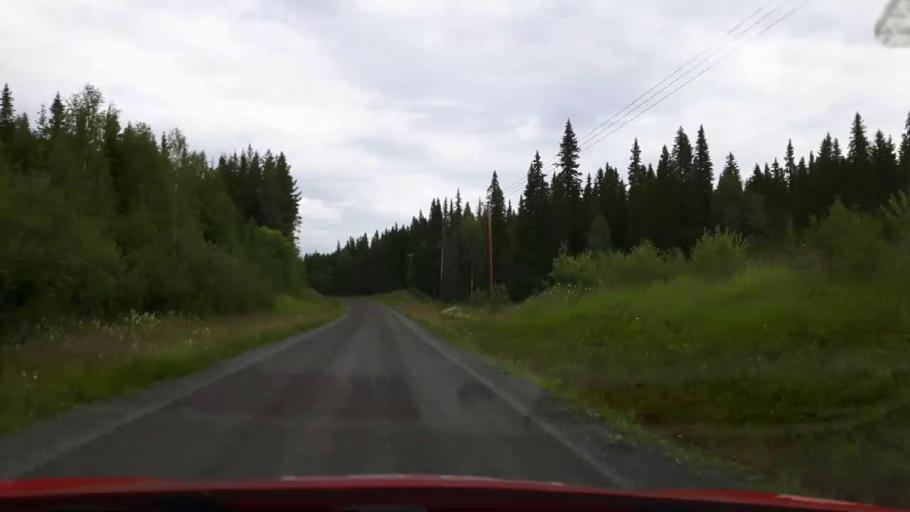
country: SE
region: Jaemtland
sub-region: Stroemsunds Kommun
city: Stroemsund
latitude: 63.4803
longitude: 15.3032
